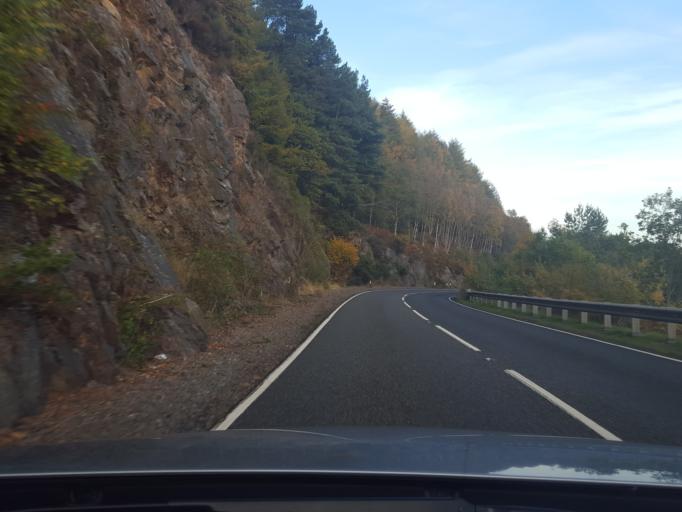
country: GB
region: Scotland
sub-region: Highland
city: Beauly
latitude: 57.3479
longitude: -4.4150
